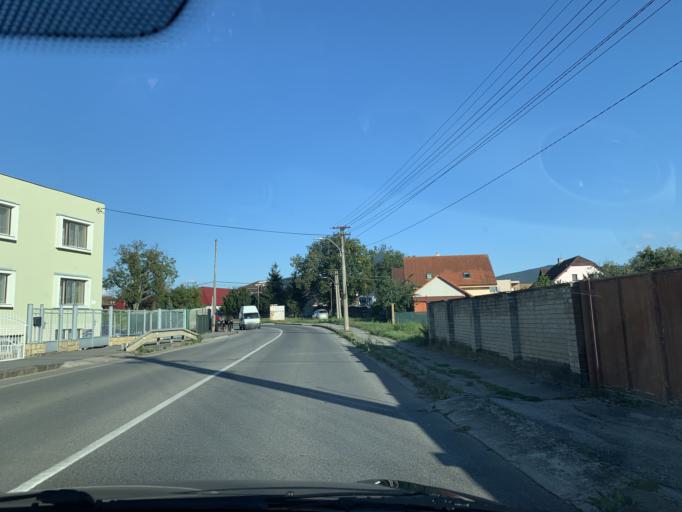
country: SK
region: Trenciansky
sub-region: Okres Trencin
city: Trencin
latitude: 48.8437
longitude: 17.9912
